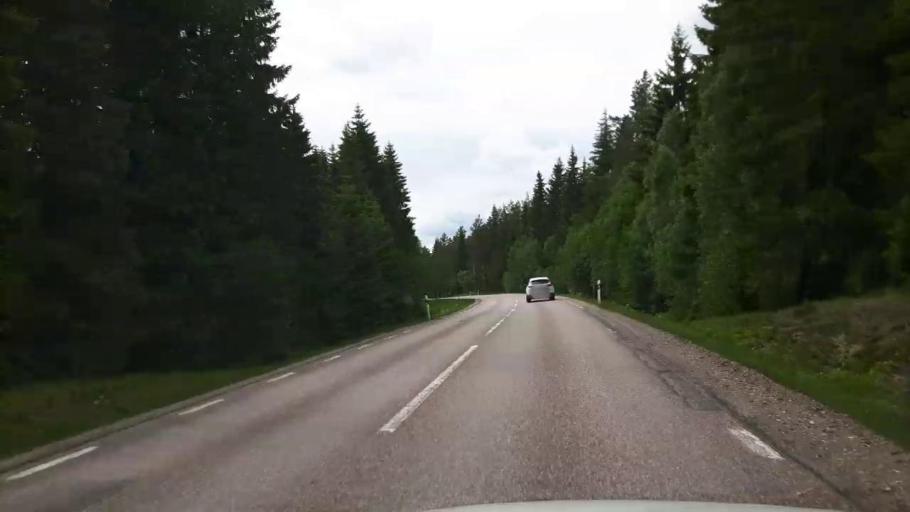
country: SE
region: Vaestmanland
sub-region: Norbergs Kommun
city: Norberg
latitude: 60.1321
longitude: 15.9381
